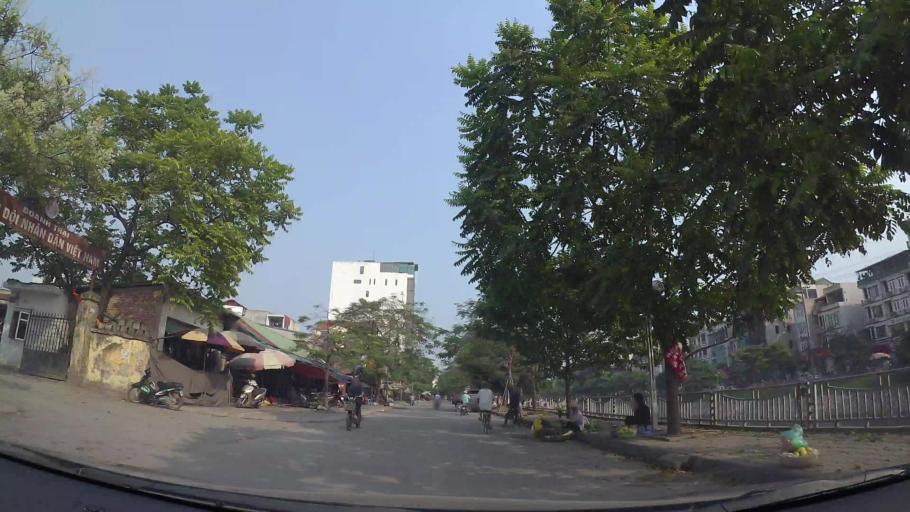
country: VN
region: Ha Noi
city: Thanh Xuan
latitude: 20.9815
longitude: 105.8178
